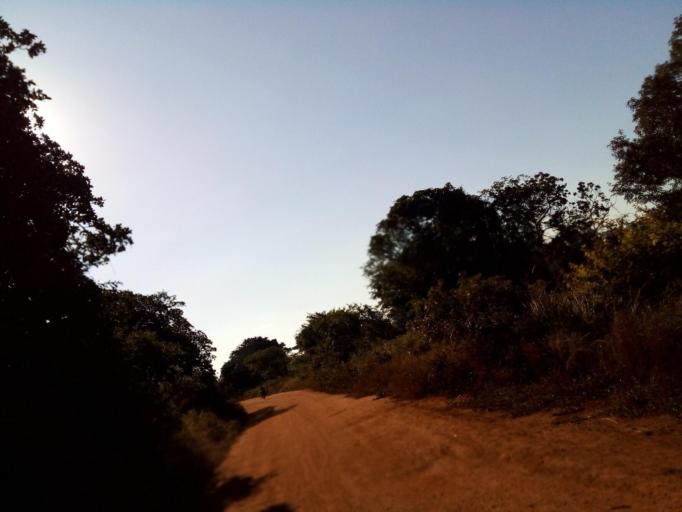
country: MZ
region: Zambezia
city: Quelimane
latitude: -17.4838
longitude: 36.5463
